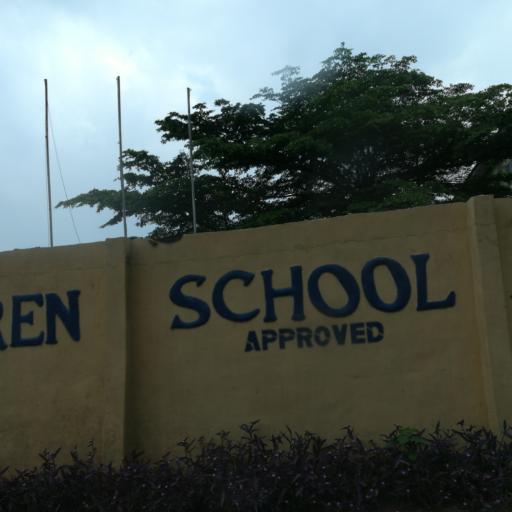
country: NG
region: Lagos
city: Agege
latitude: 6.5950
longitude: 3.2964
